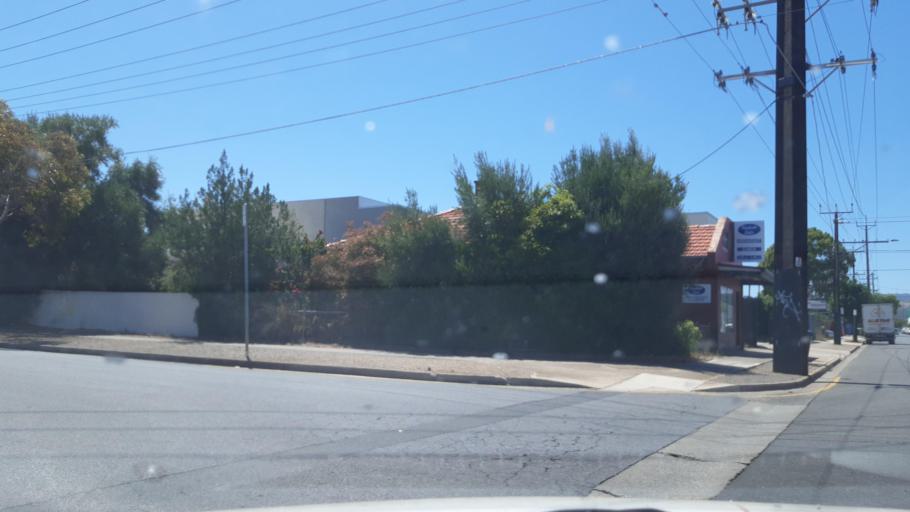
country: AU
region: South Australia
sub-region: Mitcham
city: Clarence Gardens
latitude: -34.9843
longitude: 138.5698
